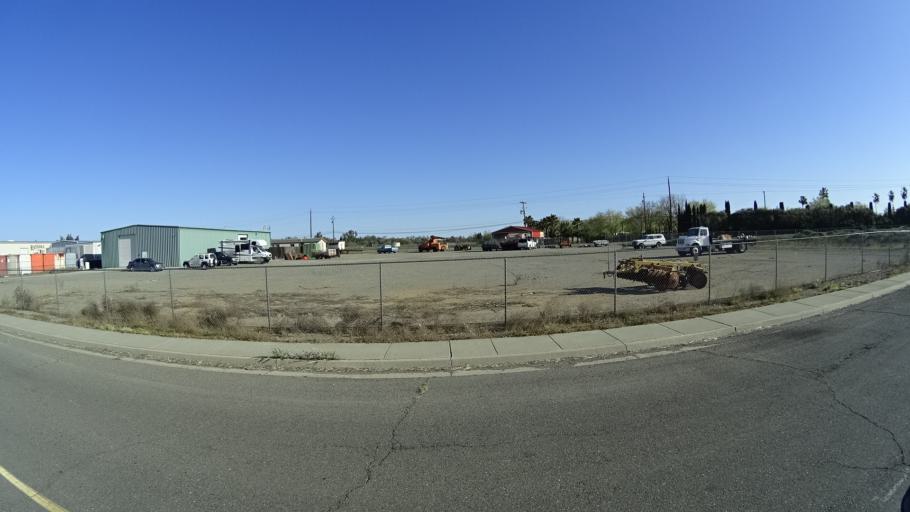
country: US
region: California
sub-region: Glenn County
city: Orland
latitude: 39.7547
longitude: -122.2184
